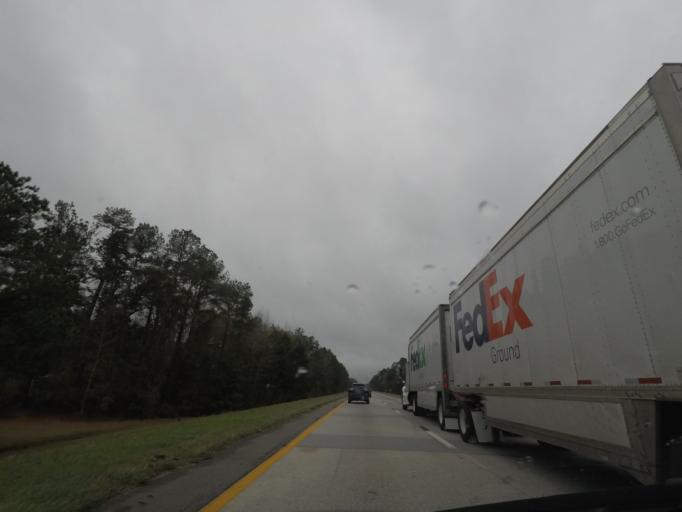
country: US
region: South Carolina
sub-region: Dorchester County
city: Saint George
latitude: 33.1091
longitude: -80.6441
